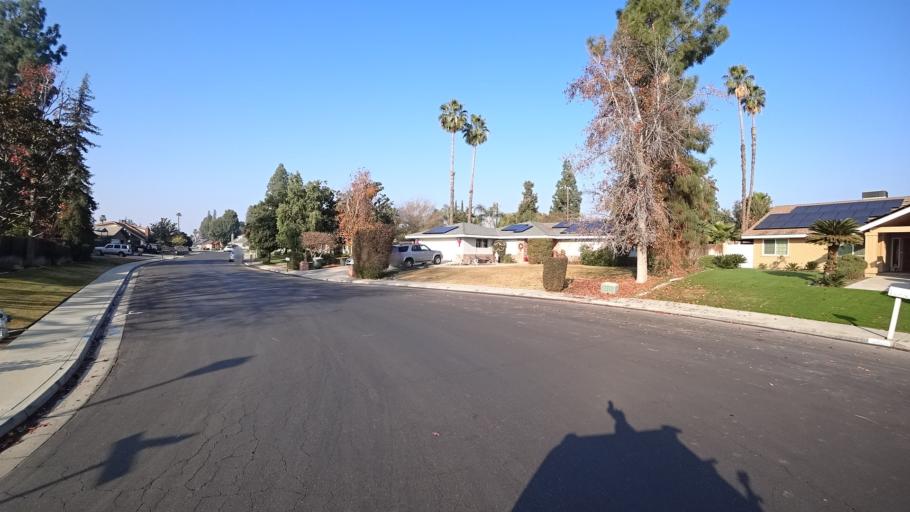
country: US
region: California
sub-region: Kern County
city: Greenacres
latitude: 35.3426
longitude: -119.0789
